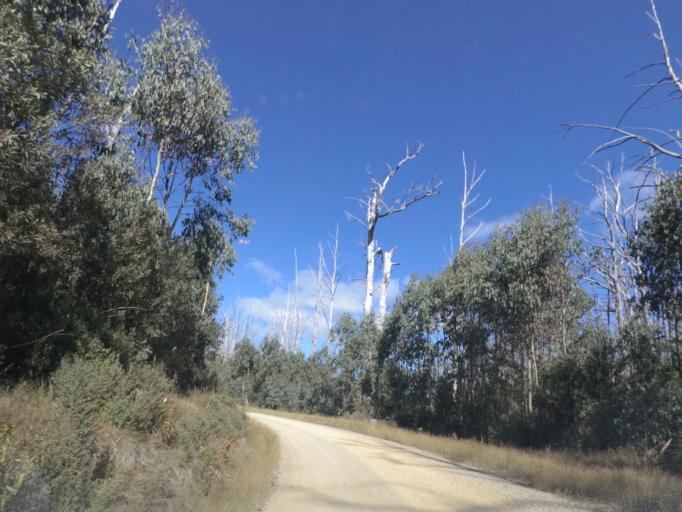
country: AU
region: Victoria
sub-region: Murrindindi
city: Alexandra
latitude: -37.4337
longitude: 145.8036
